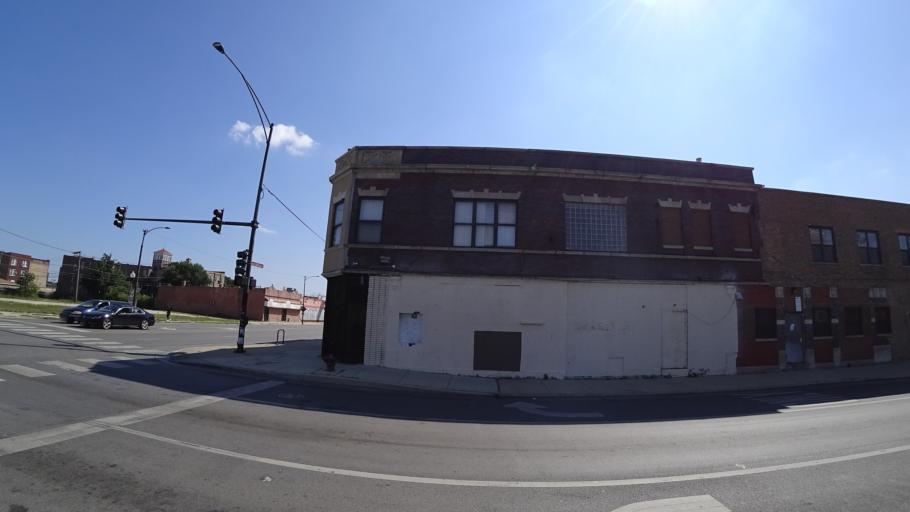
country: US
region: Illinois
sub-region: Cook County
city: Cicero
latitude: 41.8661
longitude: -87.7154
